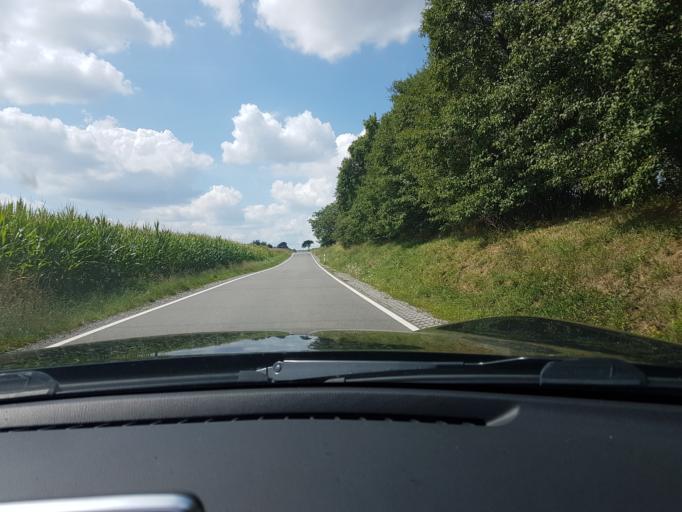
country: DE
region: Baden-Wuerttemberg
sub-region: Karlsruhe Region
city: Seckach
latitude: 49.4177
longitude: 9.2701
